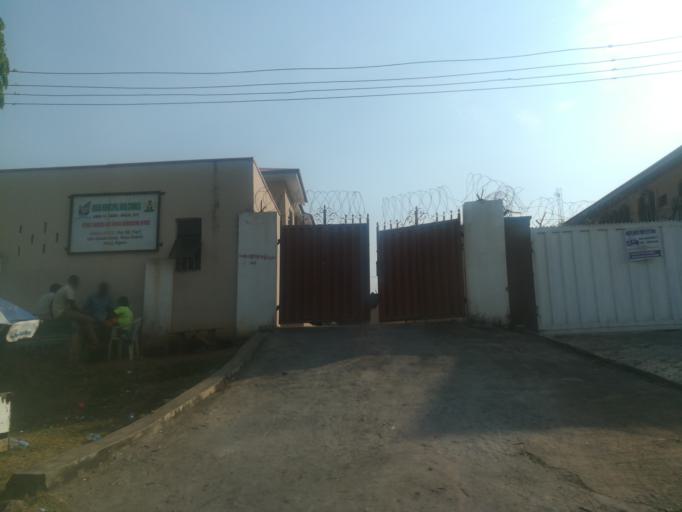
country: NG
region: Abuja Federal Capital Territory
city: Abuja
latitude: 9.0538
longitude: 7.4472
